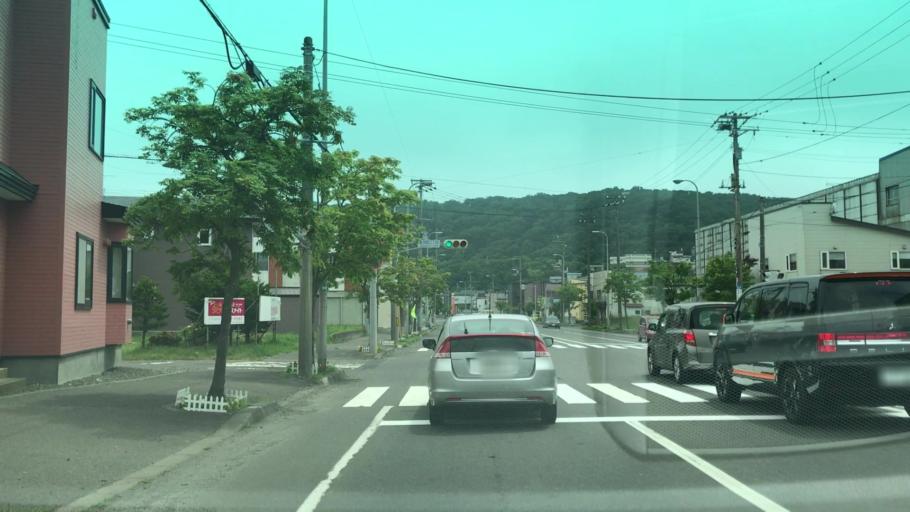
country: JP
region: Hokkaido
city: Muroran
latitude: 42.3576
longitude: 141.0452
